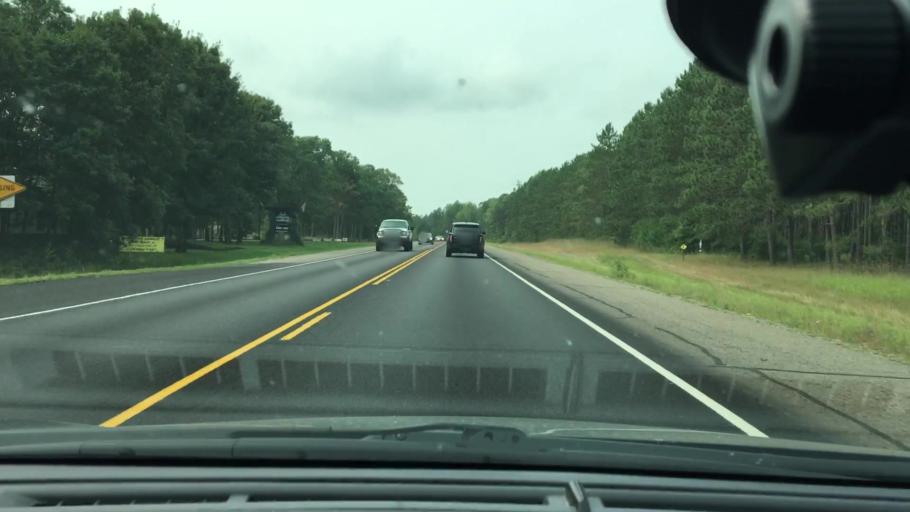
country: US
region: Minnesota
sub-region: Crow Wing County
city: Cross Lake
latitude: 46.6306
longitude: -94.1271
